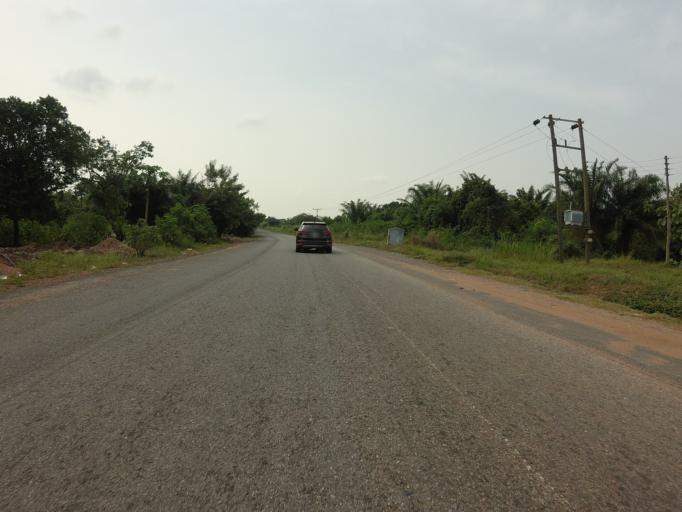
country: GH
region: Volta
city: Ho
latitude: 6.4310
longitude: 0.1906
